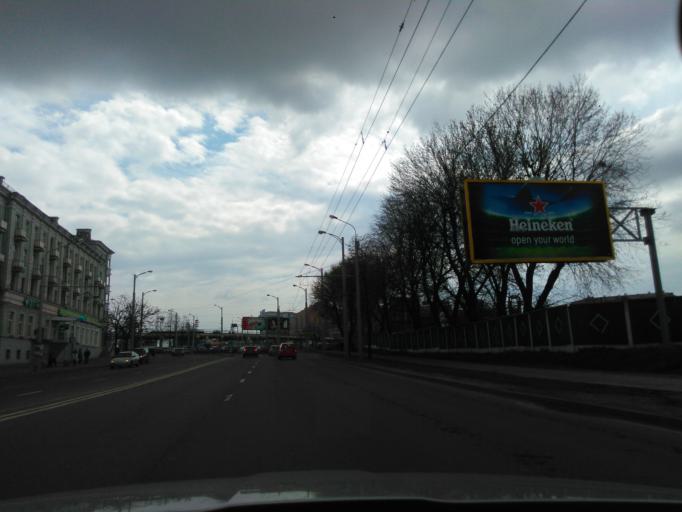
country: BY
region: Minsk
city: Minsk
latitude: 53.8944
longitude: 27.5397
